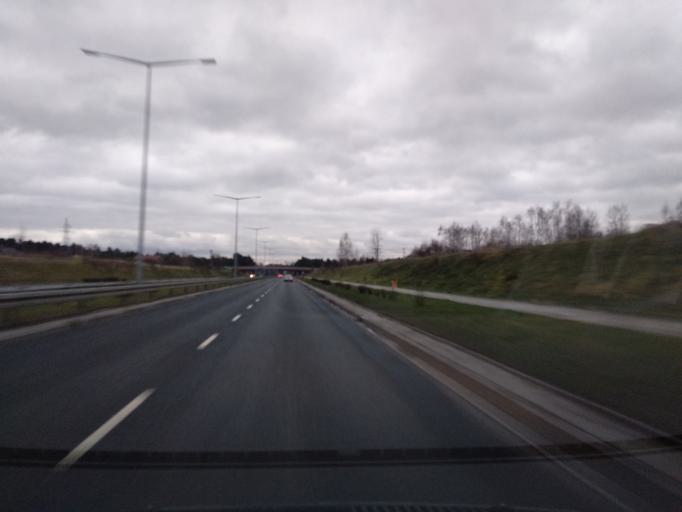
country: PL
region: Greater Poland Voivodeship
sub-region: Powiat koninski
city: Stare Miasto
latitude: 52.1959
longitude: 18.2254
